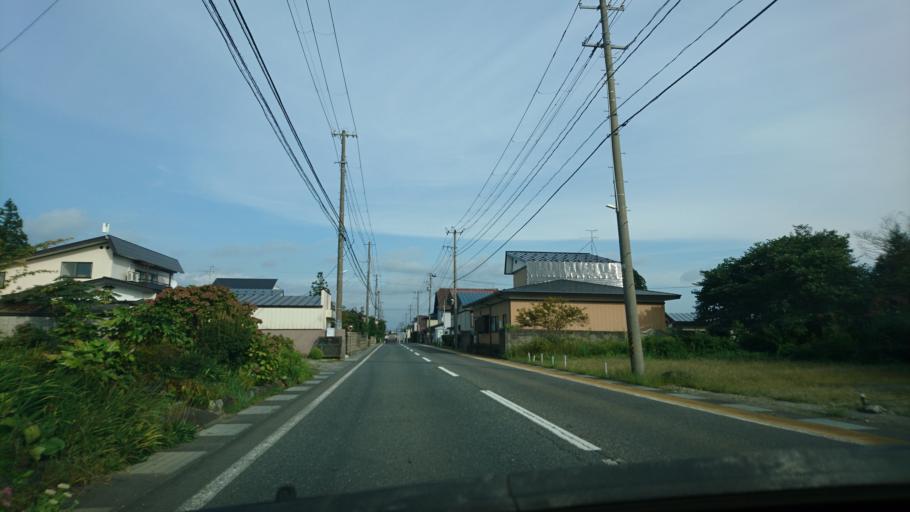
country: JP
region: Iwate
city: Kitakami
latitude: 39.3087
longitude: 140.9890
